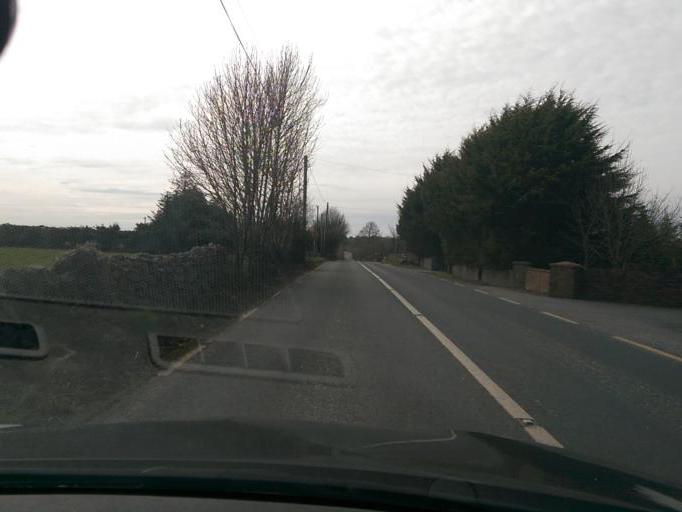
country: IE
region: Connaught
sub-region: County Galway
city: Claregalway
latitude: 53.3772
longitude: -8.8682
